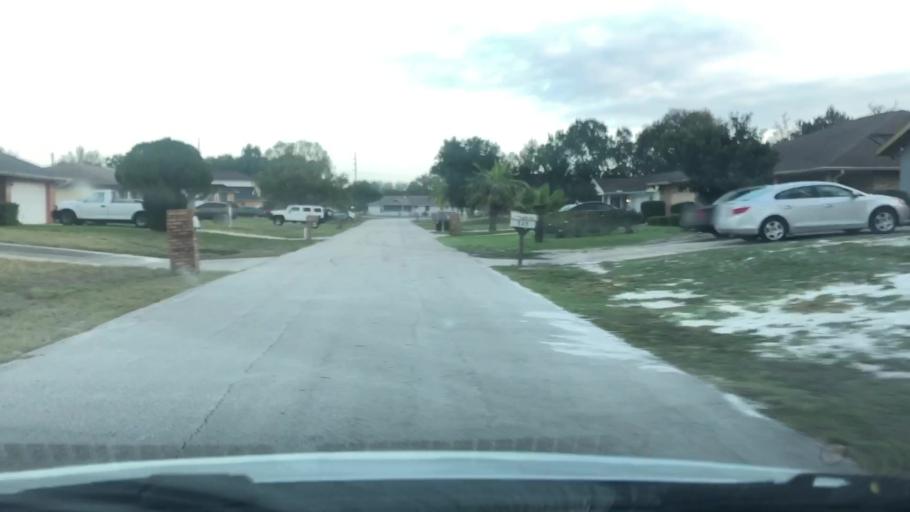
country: US
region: Florida
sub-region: Volusia County
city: Deltona
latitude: 28.8782
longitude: -81.2421
